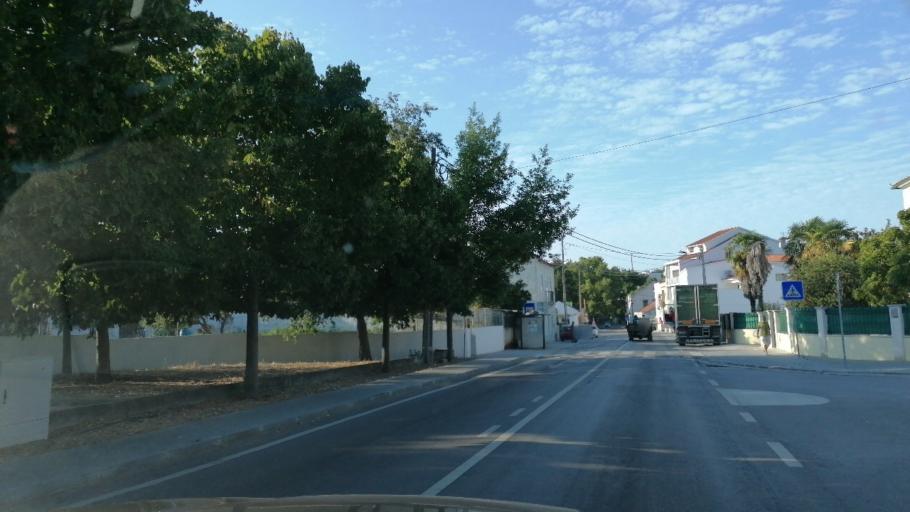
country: PT
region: Santarem
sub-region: Alcanena
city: Alcanena
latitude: 39.3787
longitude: -8.6609
